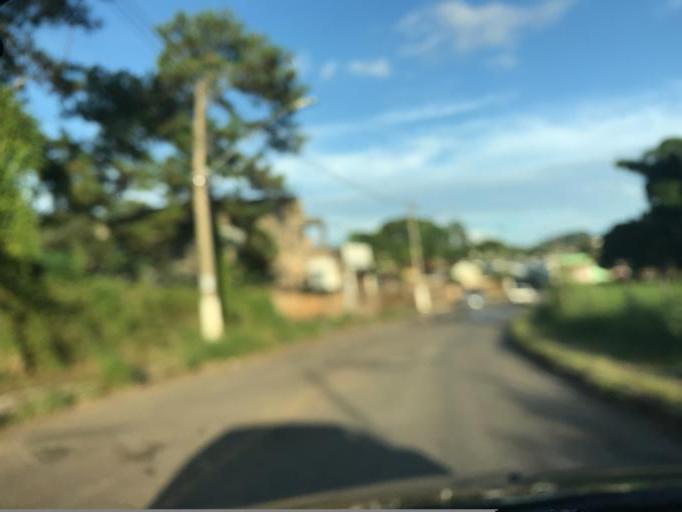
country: BR
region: Minas Gerais
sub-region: Tres Coracoes
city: Tres Coracoes
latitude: -21.6967
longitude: -45.2447
